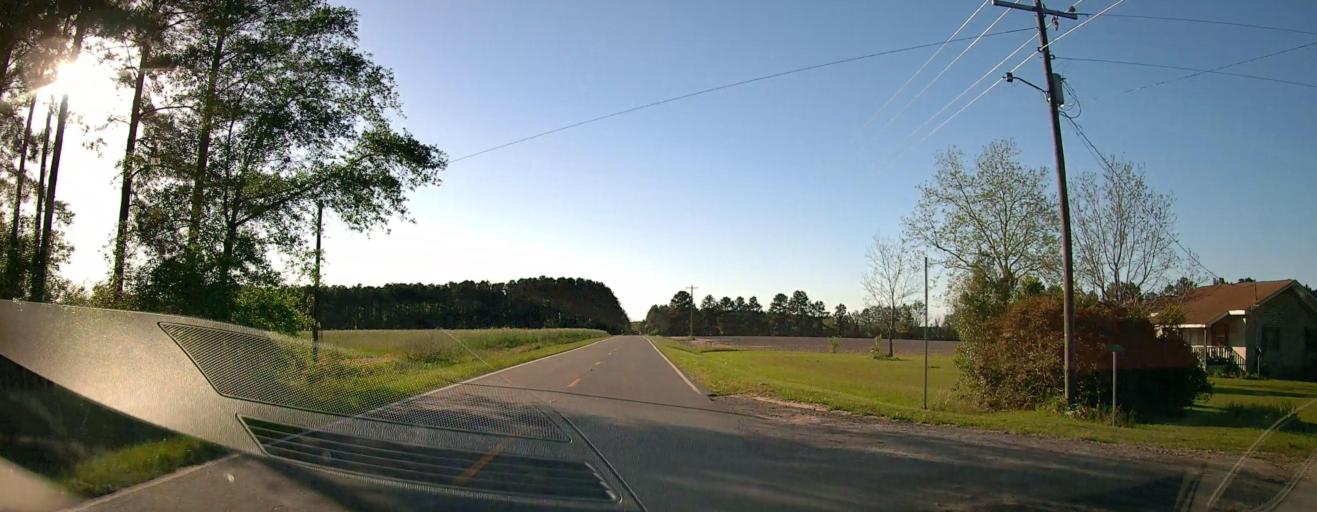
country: US
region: Georgia
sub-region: Ben Hill County
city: Fitzgerald
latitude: 31.6670
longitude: -83.1855
